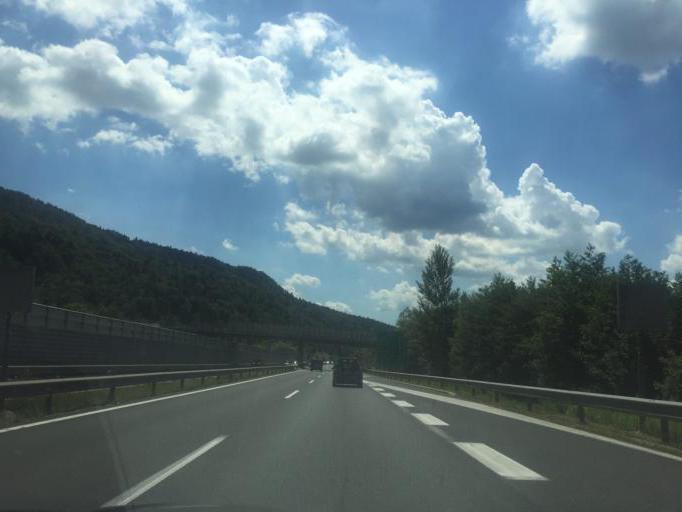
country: SI
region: Moravce
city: Moravce
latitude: 46.1691
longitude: 14.7727
